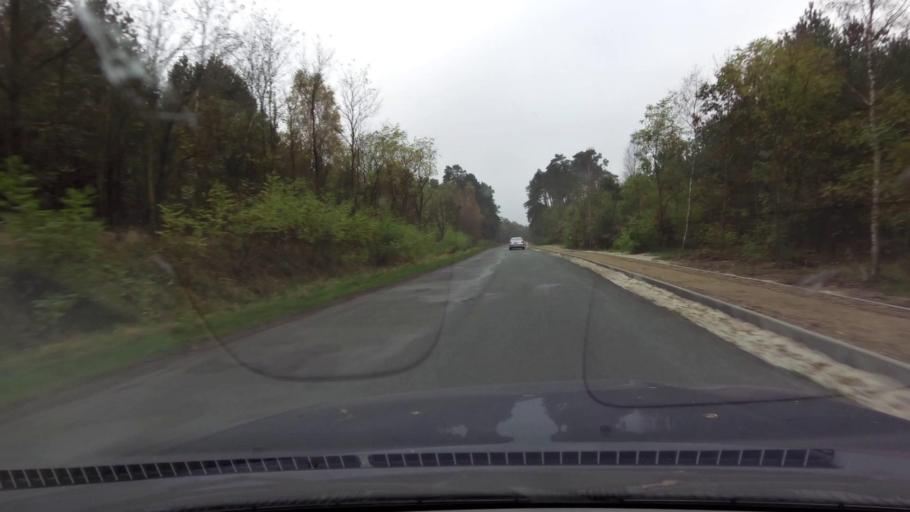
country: PL
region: West Pomeranian Voivodeship
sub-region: Powiat goleniowski
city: Goleniow
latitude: 53.5431
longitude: 14.7703
